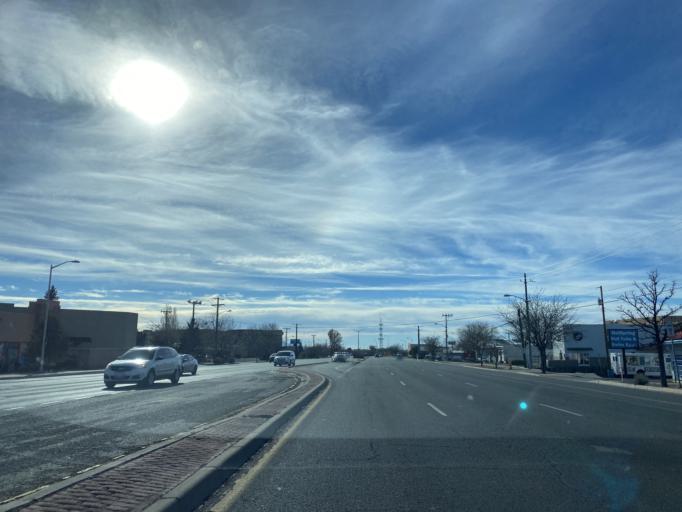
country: US
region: New Mexico
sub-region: Santa Fe County
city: Agua Fria
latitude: 35.6420
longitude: -106.0132
